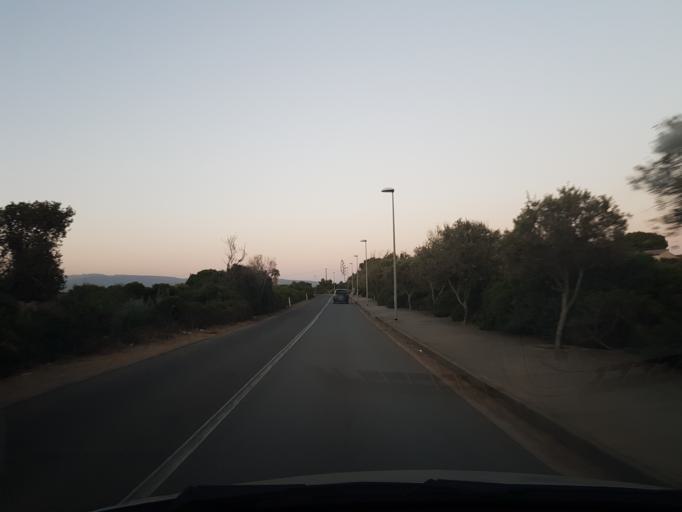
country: IT
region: Sardinia
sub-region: Provincia di Oristano
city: Riola Sardo
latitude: 40.0285
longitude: 8.4119
